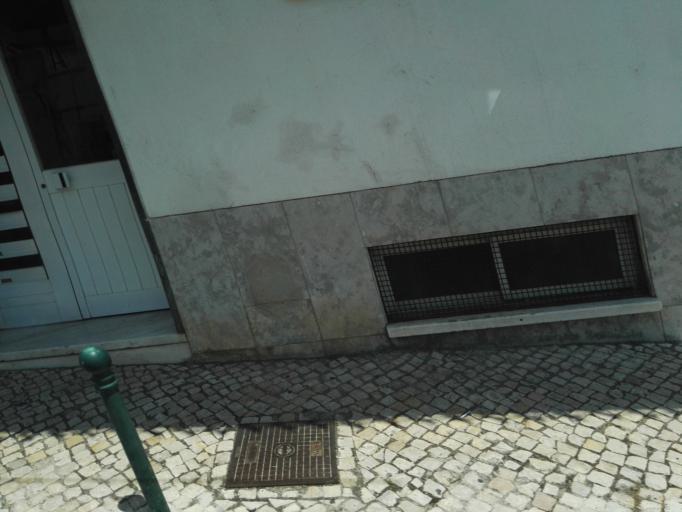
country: PT
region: Lisbon
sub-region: Oeiras
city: Terrugem
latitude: 38.7055
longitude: -9.2750
